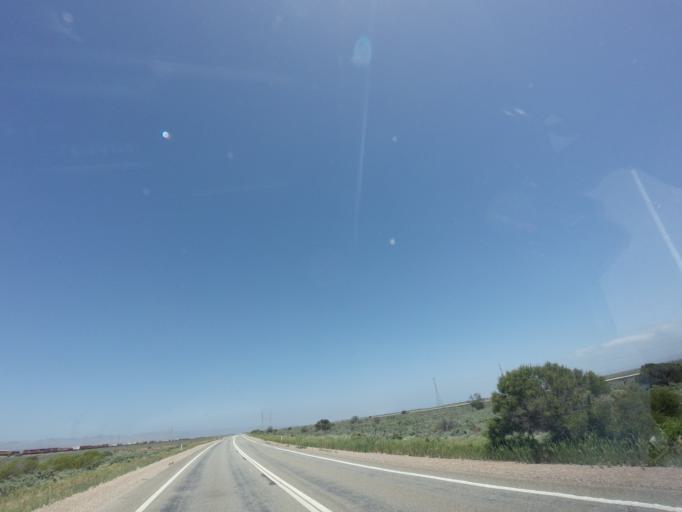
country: AU
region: South Australia
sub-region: Port Augusta
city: Port Augusta
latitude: -32.5431
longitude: 137.8564
